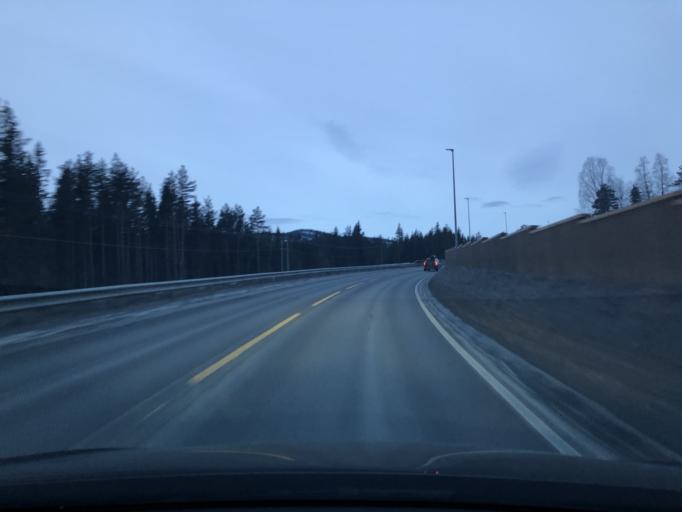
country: NO
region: Oppland
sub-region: Sor-Aurdal
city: Bagn
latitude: 60.8940
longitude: 9.4643
